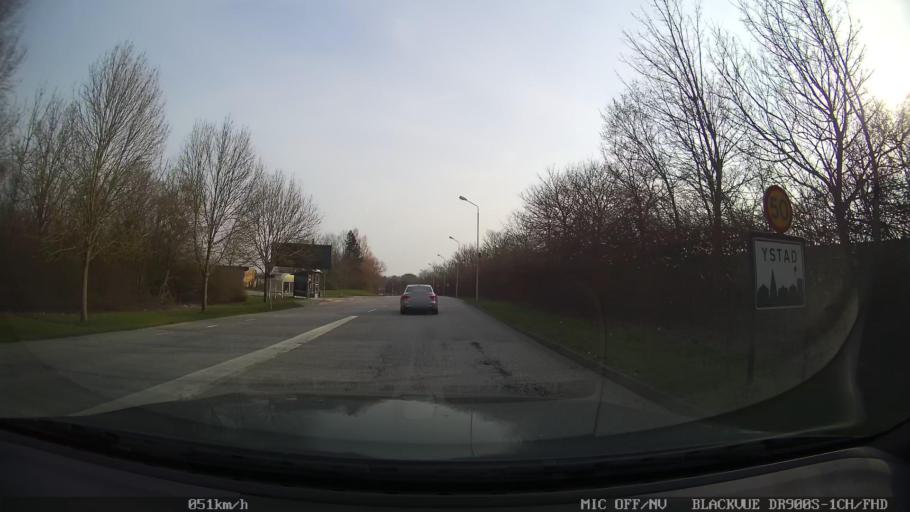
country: SE
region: Skane
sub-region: Ystads Kommun
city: Ystad
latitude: 55.4416
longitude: 13.8069
